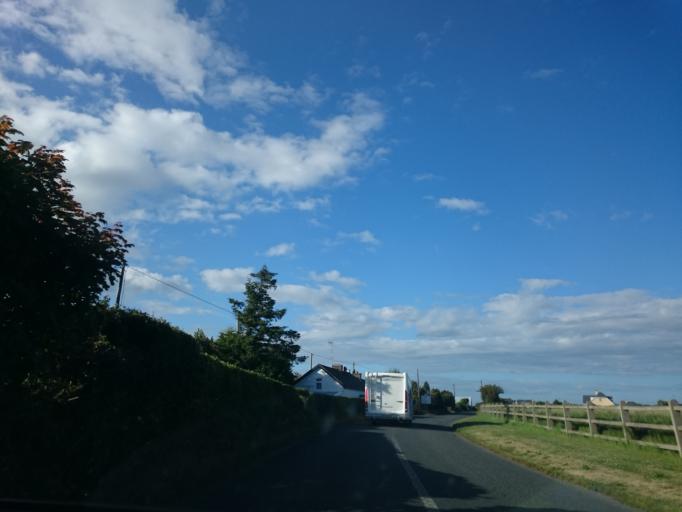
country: IE
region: Leinster
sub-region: Loch Garman
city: Loch Garman
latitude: 52.1822
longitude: -6.5817
